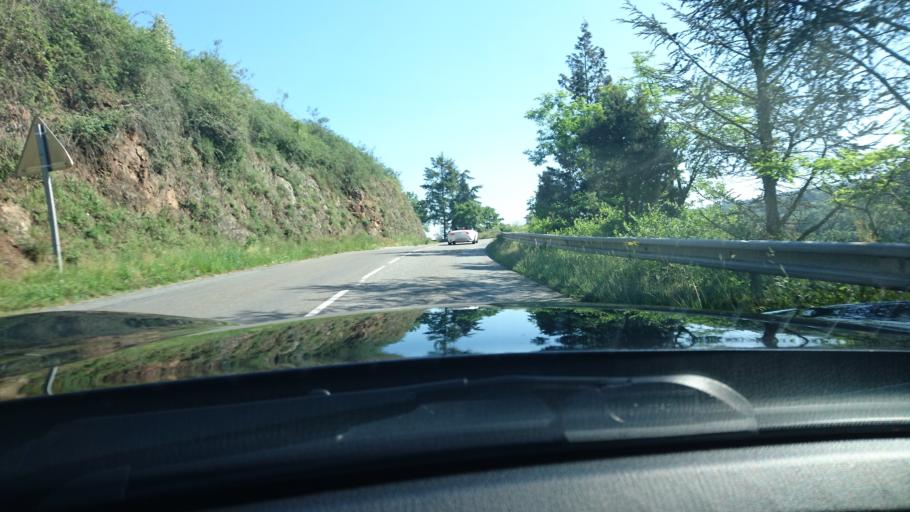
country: FR
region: Rhone-Alpes
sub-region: Departement du Rhone
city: Bessenay
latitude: 45.7740
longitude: 4.5676
